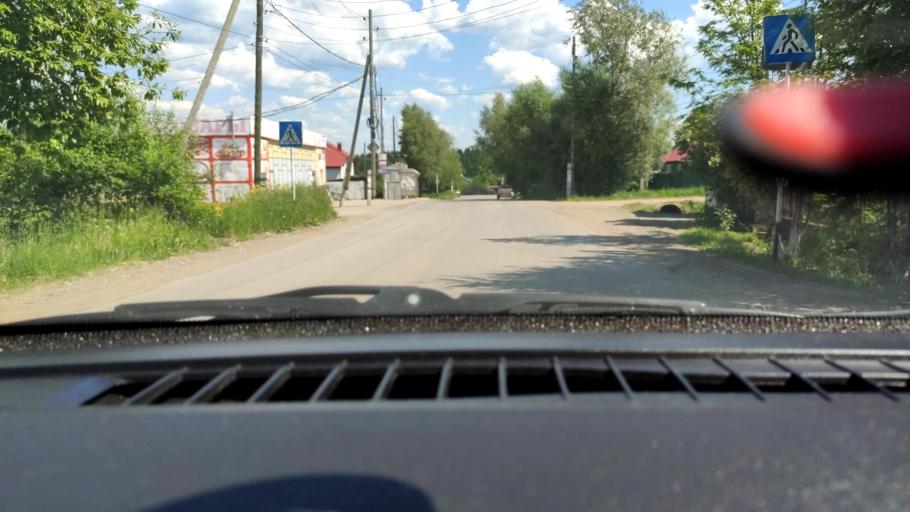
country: RU
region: Perm
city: Sylva
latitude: 58.0326
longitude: 56.7707
